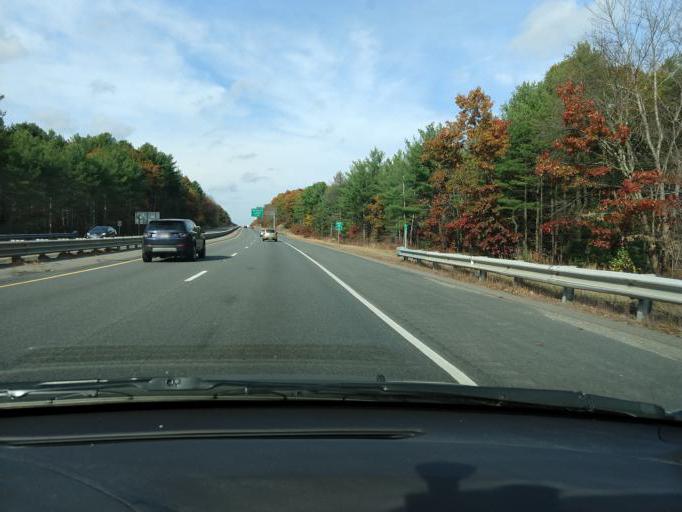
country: US
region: Massachusetts
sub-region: Middlesex County
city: Acton
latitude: 42.4941
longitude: -71.4637
